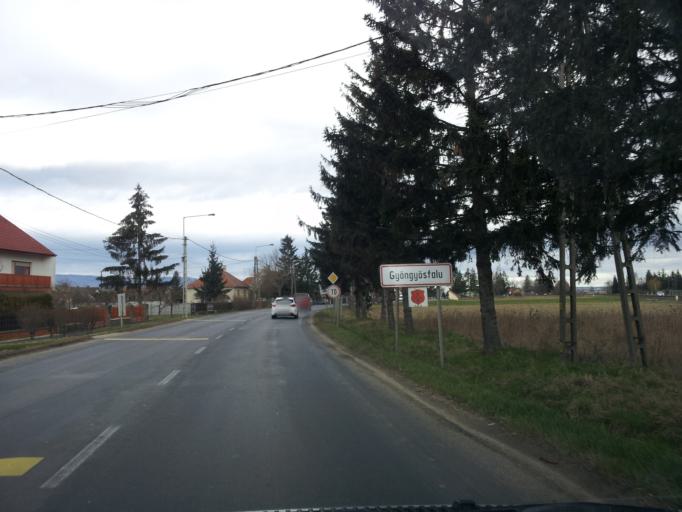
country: HU
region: Vas
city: Gencsapati
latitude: 47.3172
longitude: 16.5880
